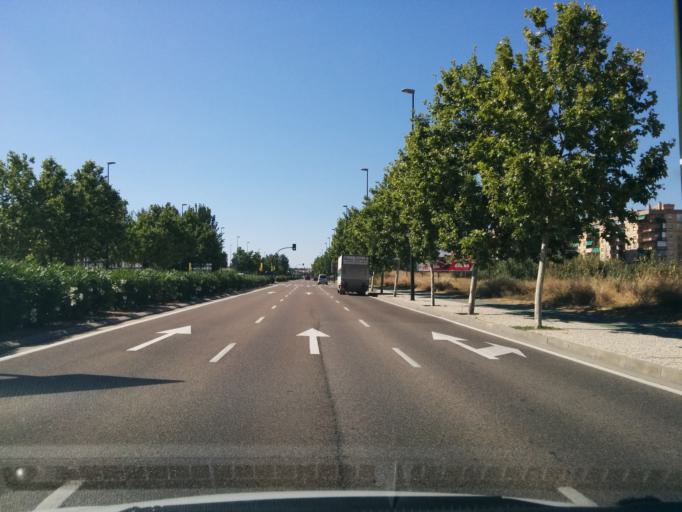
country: ES
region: Aragon
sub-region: Provincia de Zaragoza
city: Zaragoza
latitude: 41.6610
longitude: -0.8550
